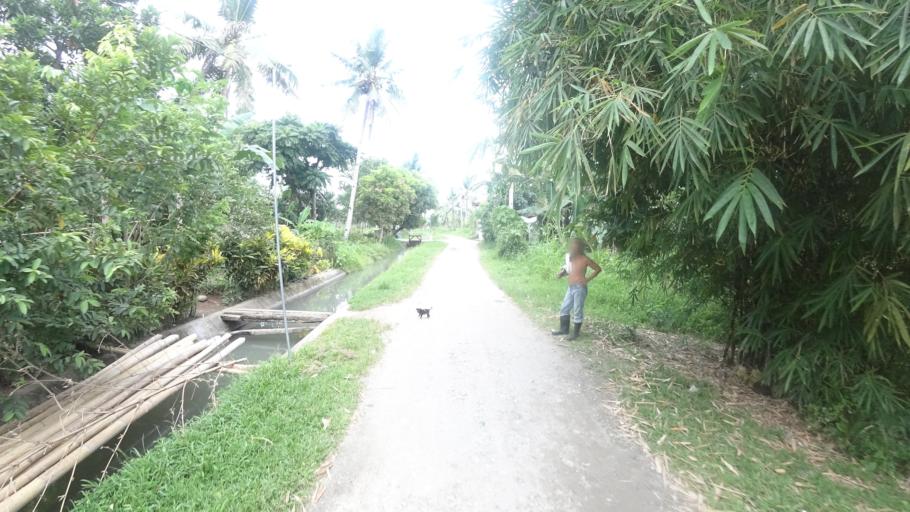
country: PH
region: Eastern Visayas
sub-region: Province of Leyte
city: MacArthur
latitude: 10.8469
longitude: 124.9639
